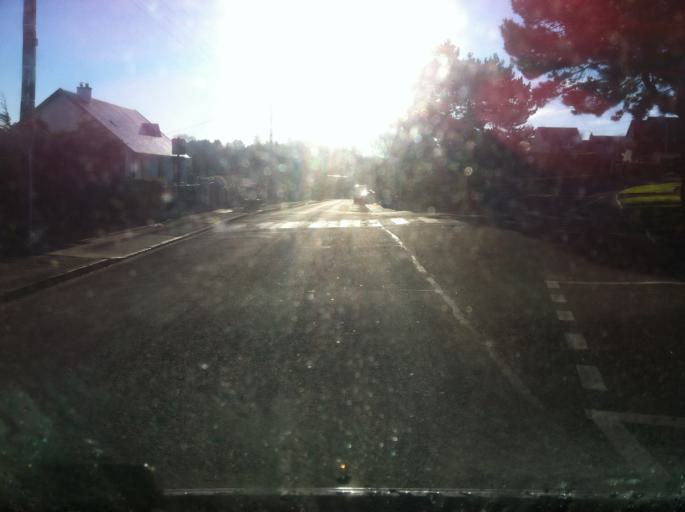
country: FR
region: Haute-Normandie
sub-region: Departement de la Seine-Maritime
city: Le Treport
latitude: 50.0563
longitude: 1.3690
